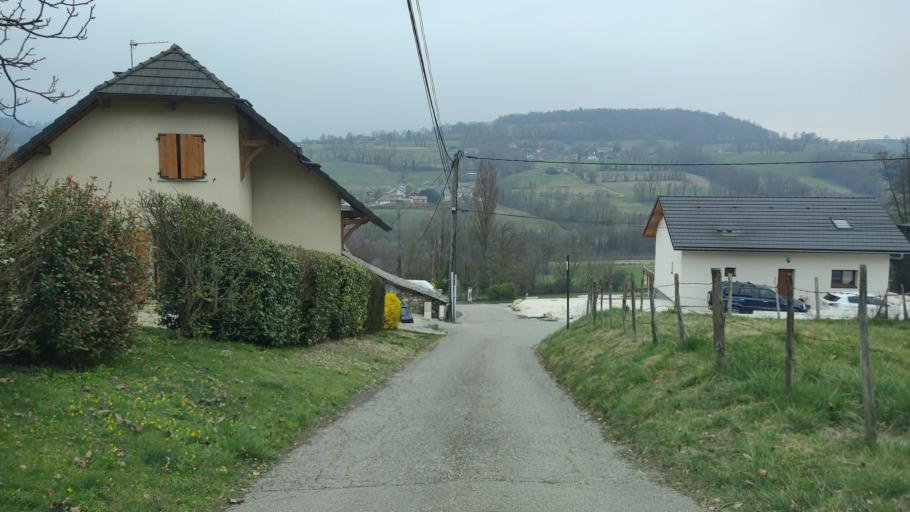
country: FR
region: Rhone-Alpes
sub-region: Departement de la Savoie
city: La Biolle
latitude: 45.7576
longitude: 5.9402
